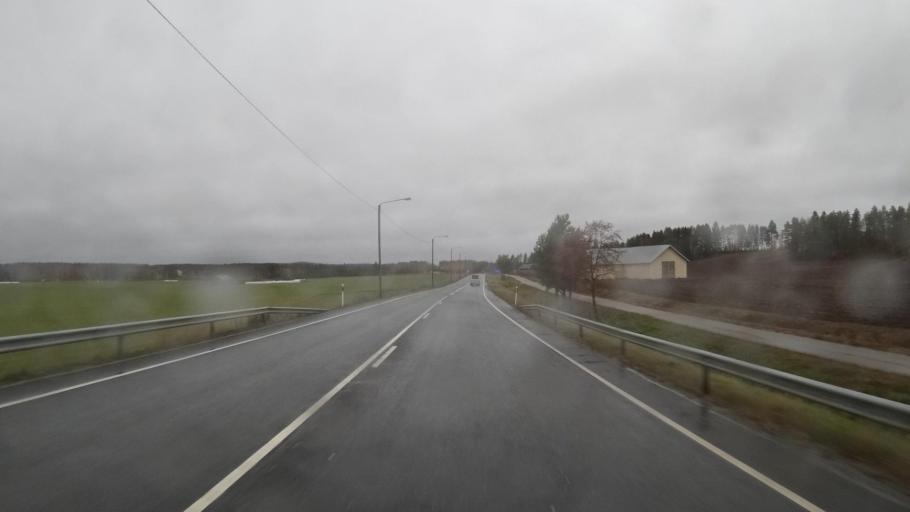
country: FI
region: Northern Savo
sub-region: Koillis-Savo
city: Tuusniemi
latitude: 62.8124
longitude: 28.4822
